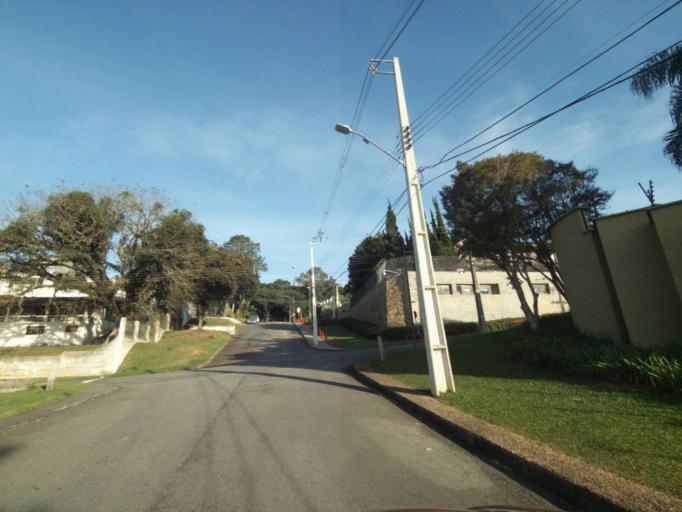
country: BR
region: Parana
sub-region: Curitiba
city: Curitiba
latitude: -25.4300
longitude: -49.3054
